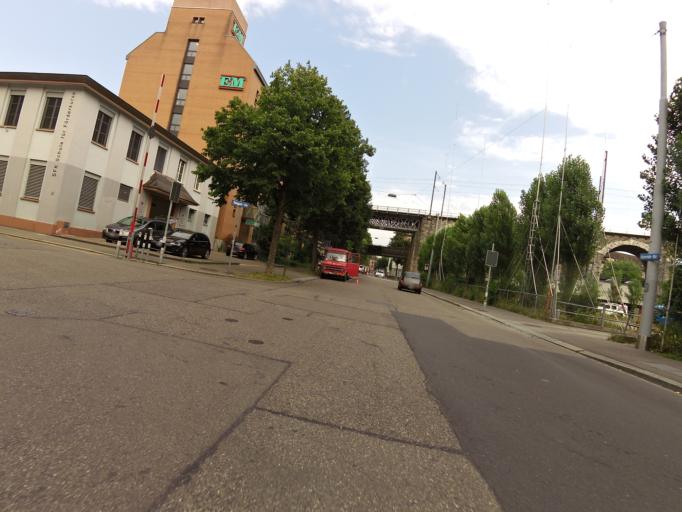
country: CH
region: Zurich
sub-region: Bezirk Zuerich
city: Zuerich (Kreis 5)
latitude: 47.3879
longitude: 8.5246
